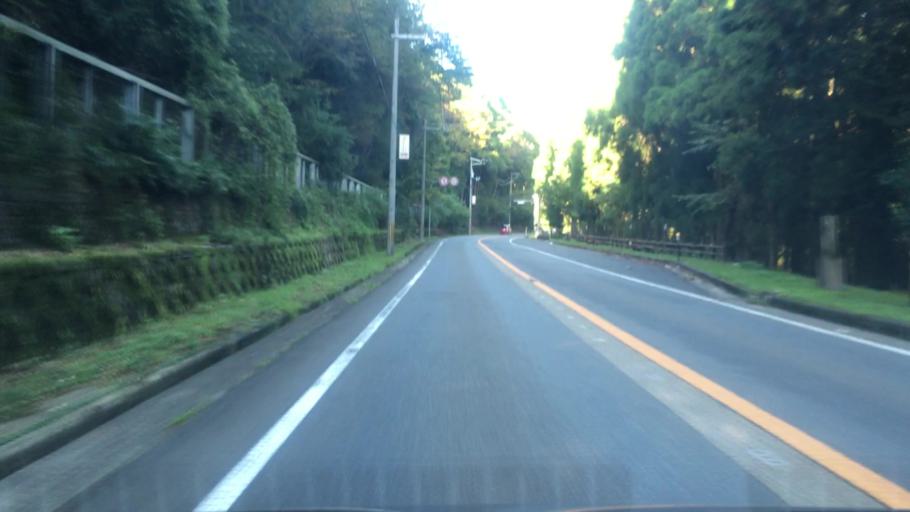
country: JP
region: Hyogo
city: Toyooka
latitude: 35.5798
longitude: 134.8566
